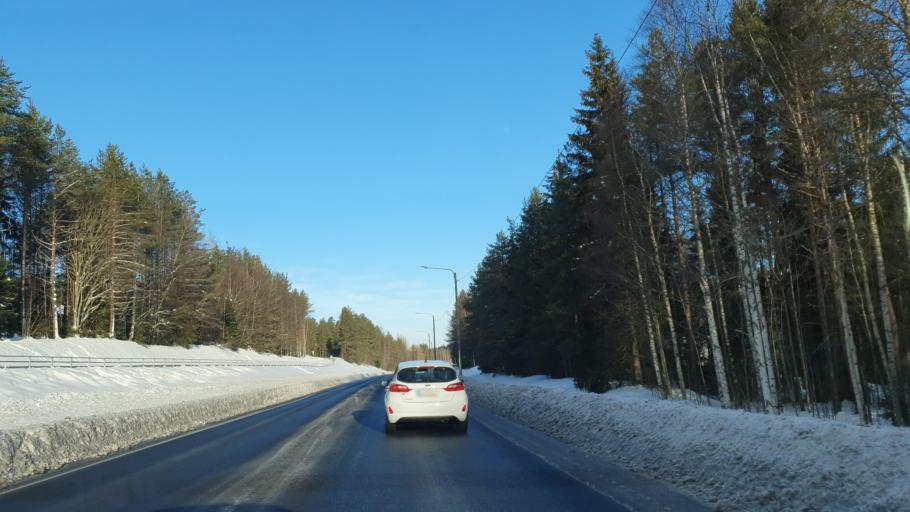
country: FI
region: Northern Ostrobothnia
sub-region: Oulu
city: Muhos
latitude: 64.8372
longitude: 25.9089
